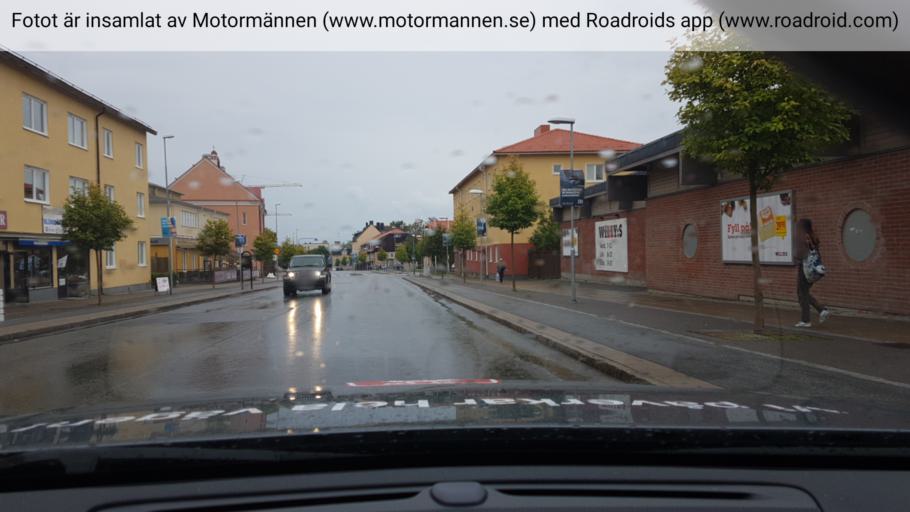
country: SE
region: Stockholm
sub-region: Nynashamns Kommun
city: Nynashamn
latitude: 58.9132
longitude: 17.9478
